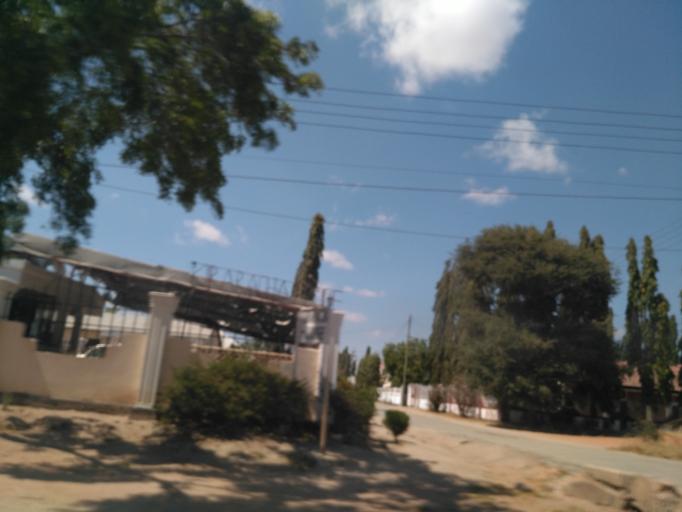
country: TZ
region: Dodoma
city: Dodoma
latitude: -6.1678
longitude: 35.7580
